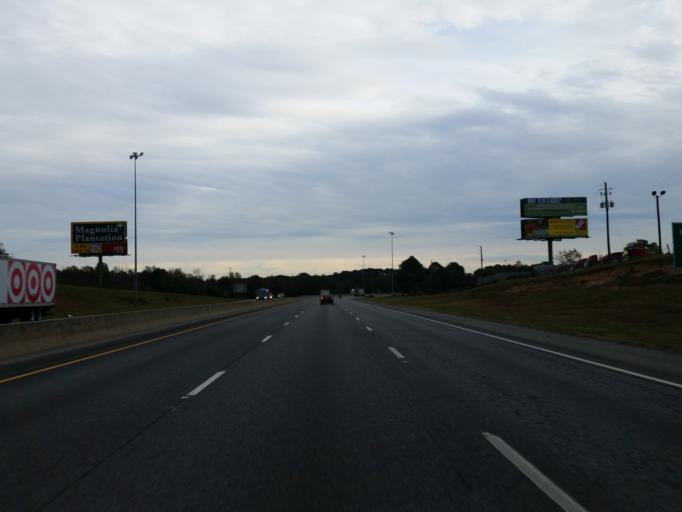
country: US
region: Georgia
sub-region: Tift County
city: Unionville
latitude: 31.4245
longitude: -83.5104
